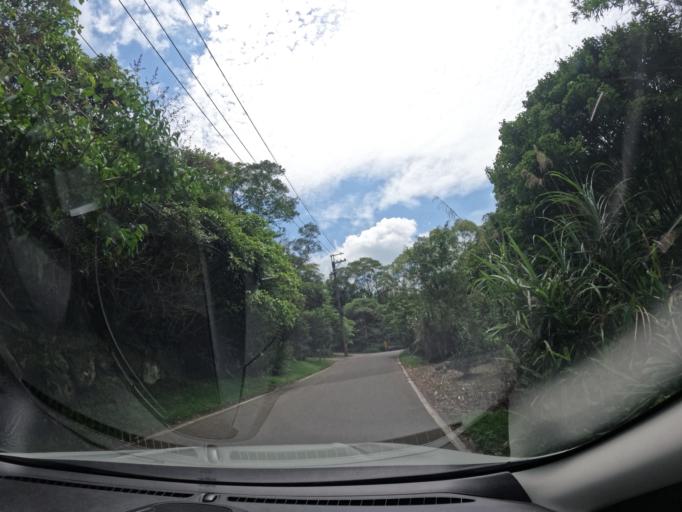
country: TW
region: Taipei
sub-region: Taipei
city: Banqiao
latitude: 24.9112
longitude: 121.4089
